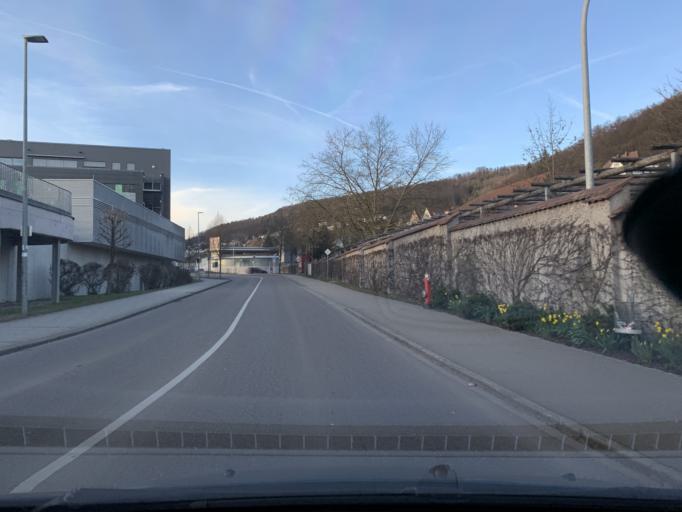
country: DE
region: Baden-Wuerttemberg
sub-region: Freiburg Region
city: Waldshut-Tiengen
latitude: 47.6227
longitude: 8.2193
